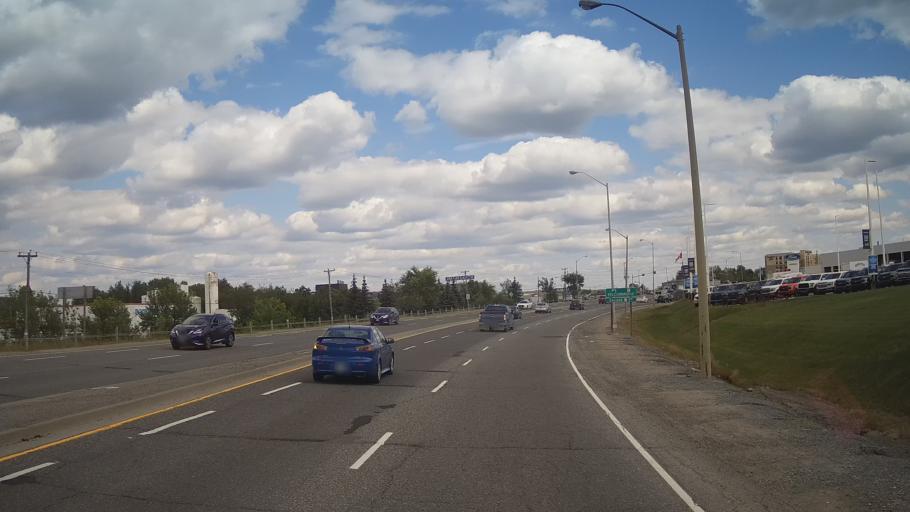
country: CA
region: Ontario
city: Greater Sudbury
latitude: 46.5060
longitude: -80.9421
